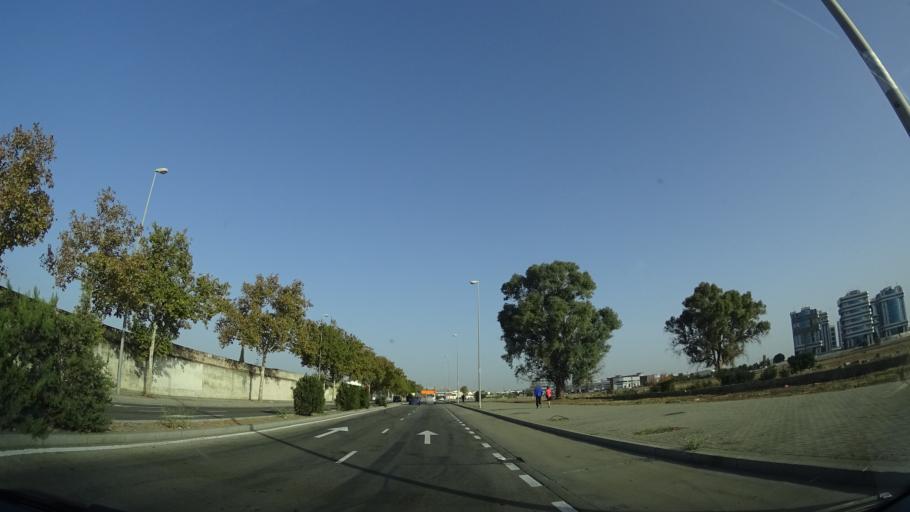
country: ES
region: Andalusia
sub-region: Provincia de Sevilla
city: Sevilla
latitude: 37.4215
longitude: -5.9771
